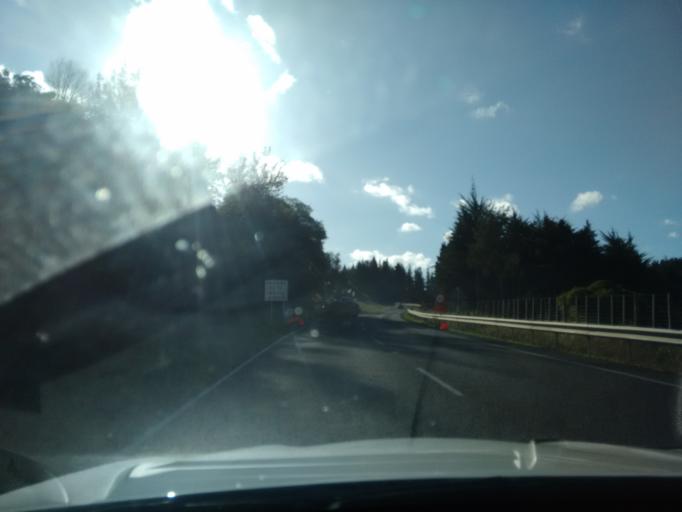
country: NZ
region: Manawatu-Wanganui
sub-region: Wanganui District
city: Wanganui
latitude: -39.8444
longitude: 174.9245
